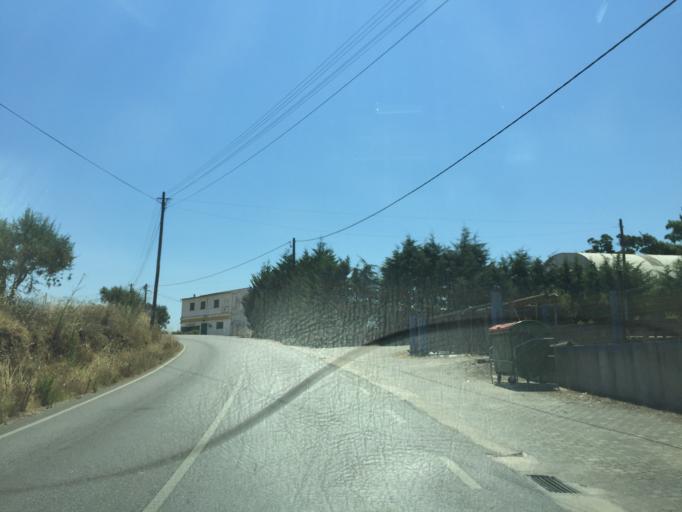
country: PT
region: Santarem
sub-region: Ferreira do Zezere
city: Ferreira do Zezere
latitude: 39.6014
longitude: -8.3072
